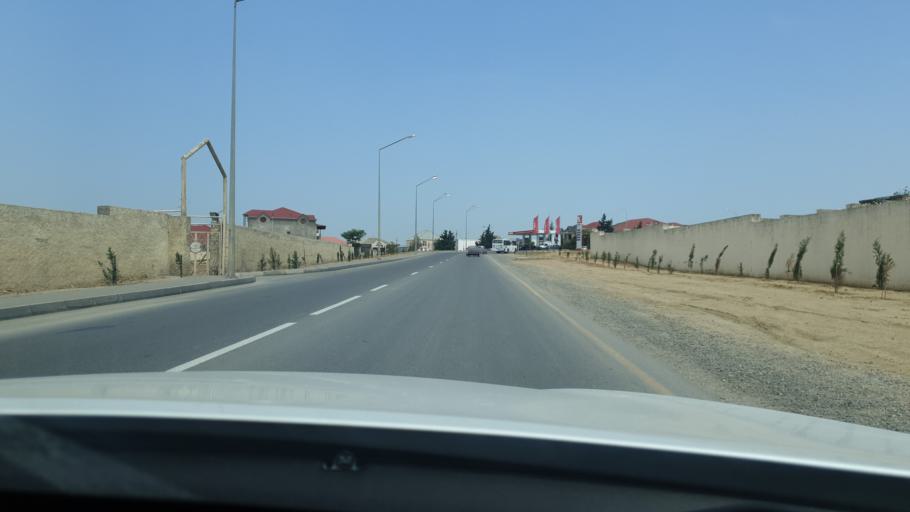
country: AZ
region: Baki
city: Qaracuxur
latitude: 40.3923
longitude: 49.9886
